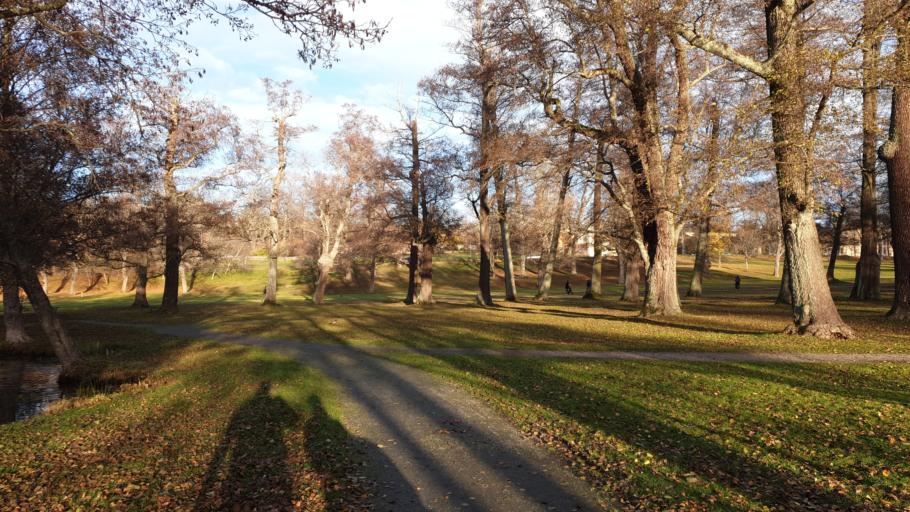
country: SE
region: Stockholm
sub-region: Stockholms Kommun
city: Bromma
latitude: 59.3240
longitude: 17.8830
